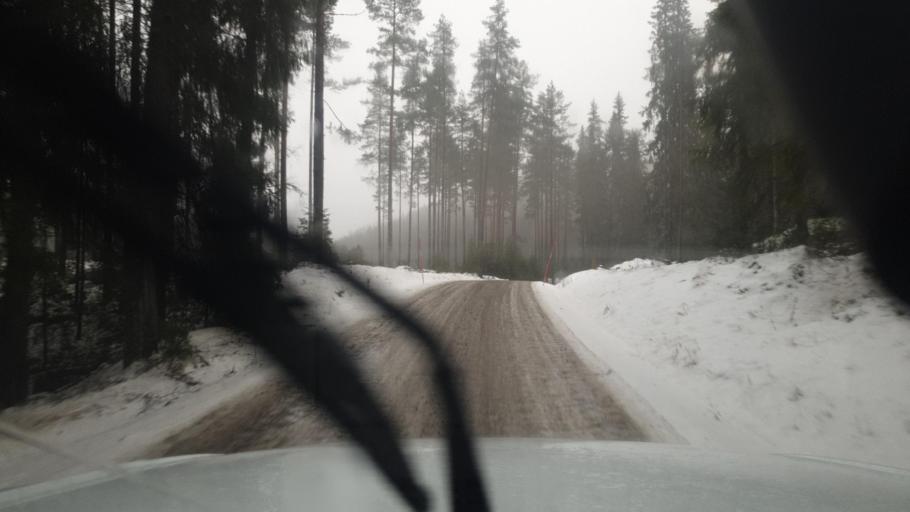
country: SE
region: Vaermland
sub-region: Eda Kommun
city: Charlottenberg
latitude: 60.0346
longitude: 12.5963
